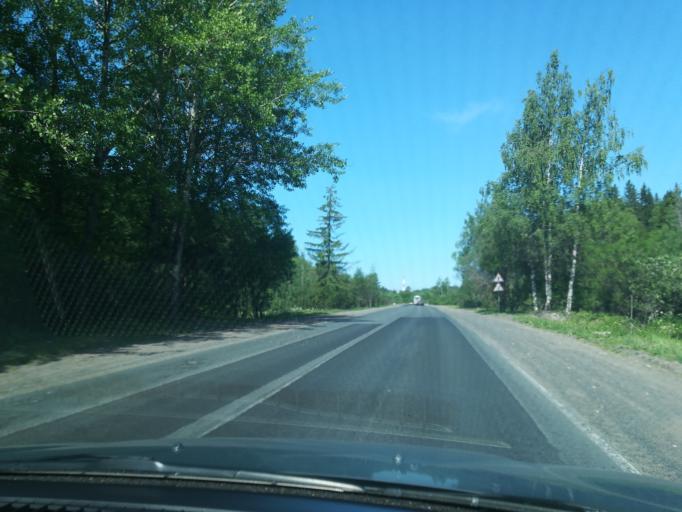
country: RU
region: Leningrad
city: Svetogorsk
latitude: 61.0911
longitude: 28.8975
